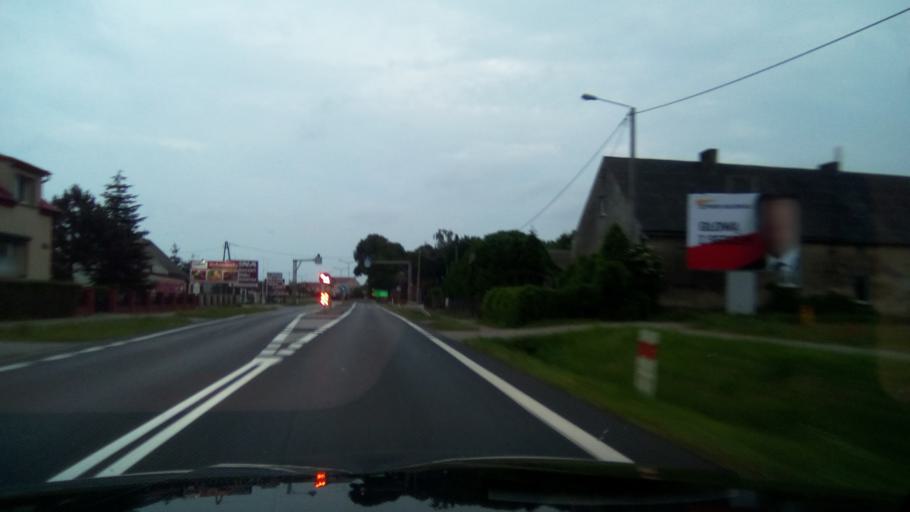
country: PL
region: Greater Poland Voivodeship
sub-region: Powiat gnieznienski
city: Lubowo
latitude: 52.5118
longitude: 17.4486
